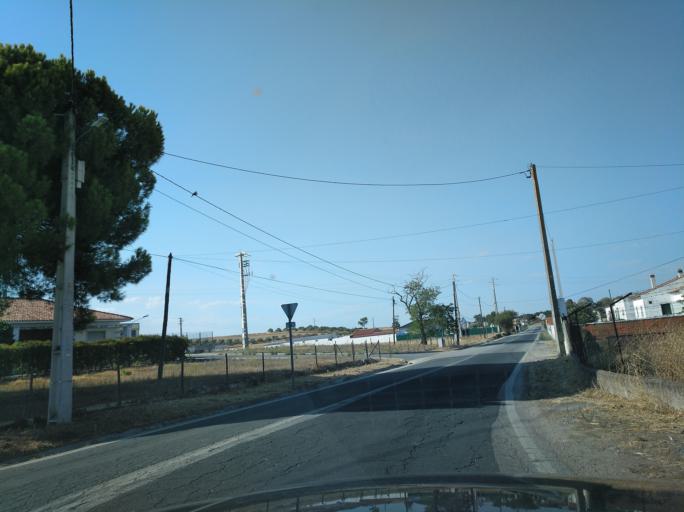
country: ES
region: Extremadura
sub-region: Provincia de Badajoz
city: Valencia del Mombuey
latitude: 38.2140
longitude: -7.2249
